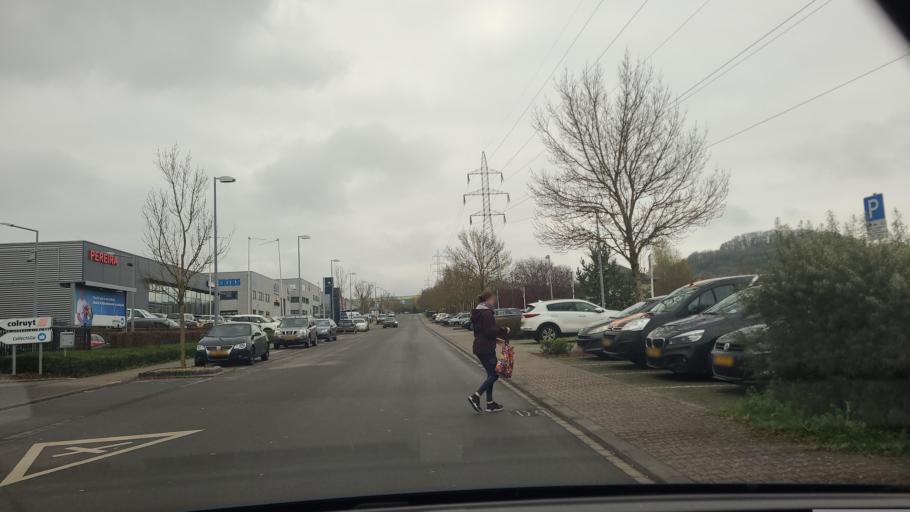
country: LU
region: Luxembourg
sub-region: Canton d'Esch-sur-Alzette
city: Sanem
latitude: 49.5373
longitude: 5.9352
